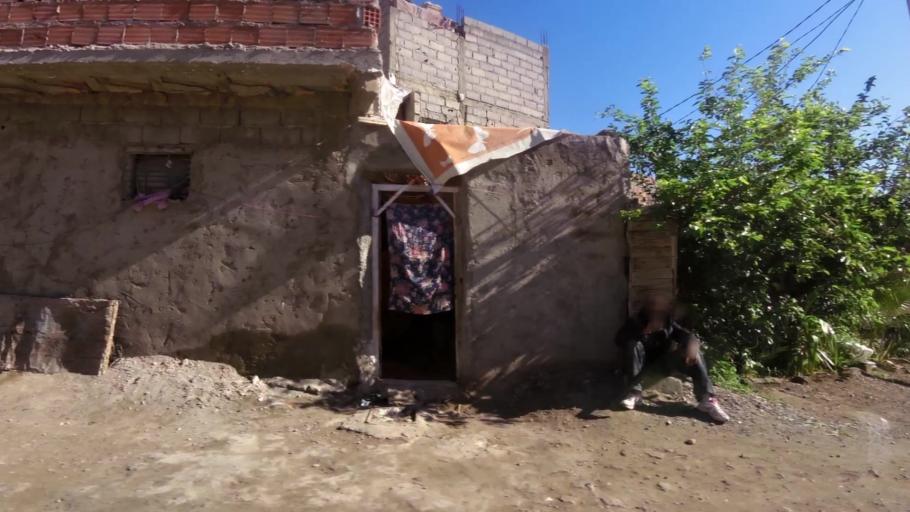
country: MA
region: Marrakech-Tensift-Al Haouz
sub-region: Marrakech
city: Marrakesh
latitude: 31.6000
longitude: -8.0309
